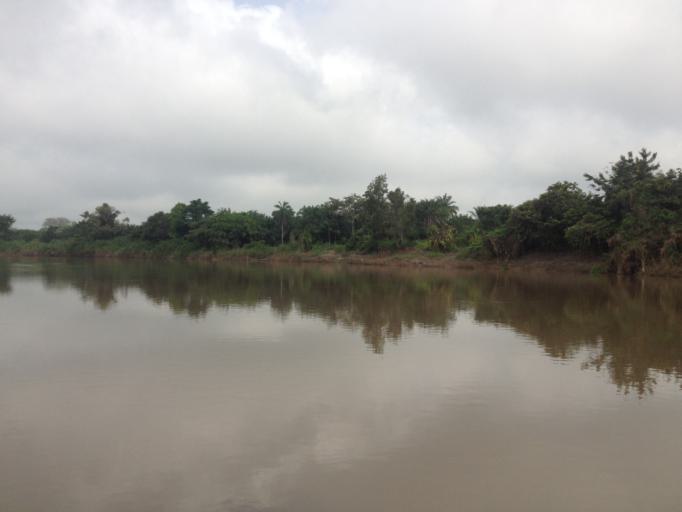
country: BJ
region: Mono
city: Come
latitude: 6.3944
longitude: 1.7723
